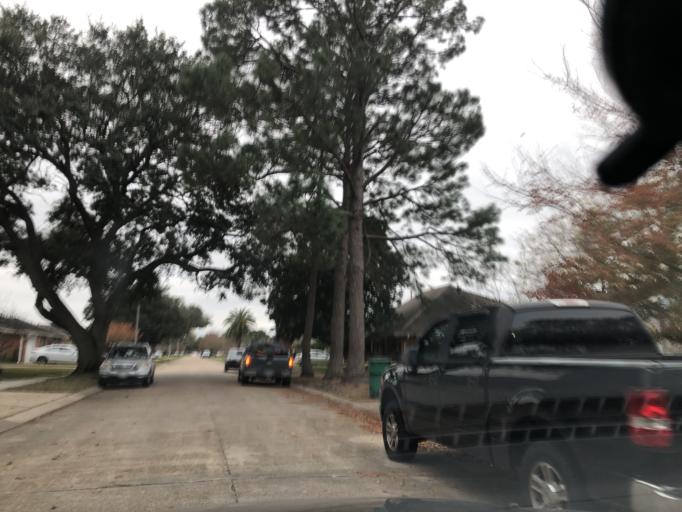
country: US
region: Louisiana
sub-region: Jefferson Parish
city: Metairie Terrace
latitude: 29.9875
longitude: -90.1683
